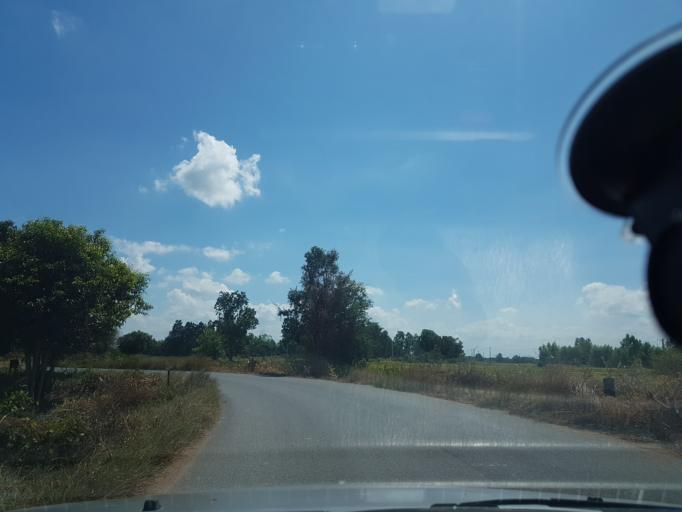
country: TH
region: Lop Buri
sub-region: Amphoe Tha Luang
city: Tha Luang
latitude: 14.9997
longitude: 101.0057
